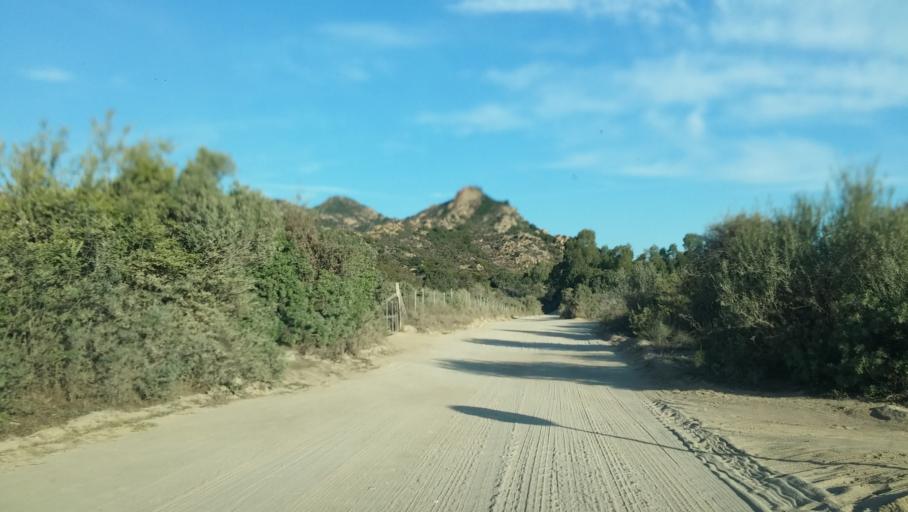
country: IT
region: Sardinia
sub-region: Provincia di Nuoro
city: La Caletta
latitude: 40.4828
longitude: 9.8035
